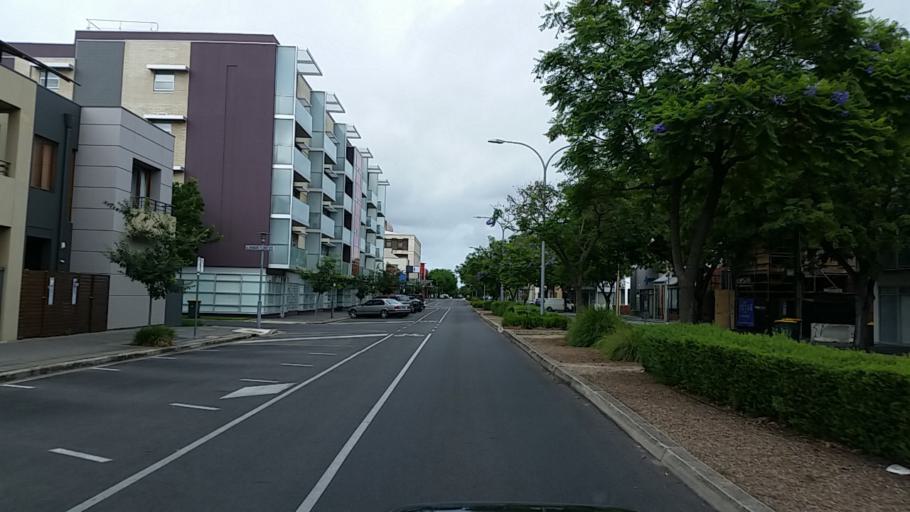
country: AU
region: South Australia
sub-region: Adelaide
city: Adelaide
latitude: -34.9328
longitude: 138.6028
